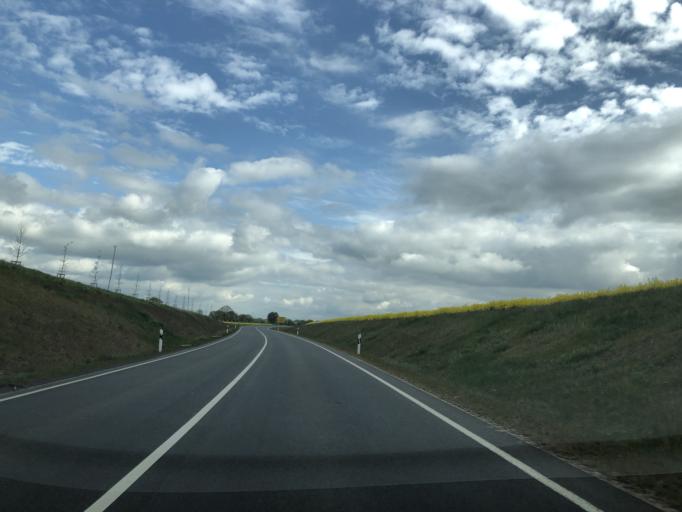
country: DE
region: Mecklenburg-Vorpommern
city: Plau am See
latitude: 53.4641
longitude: 12.2490
